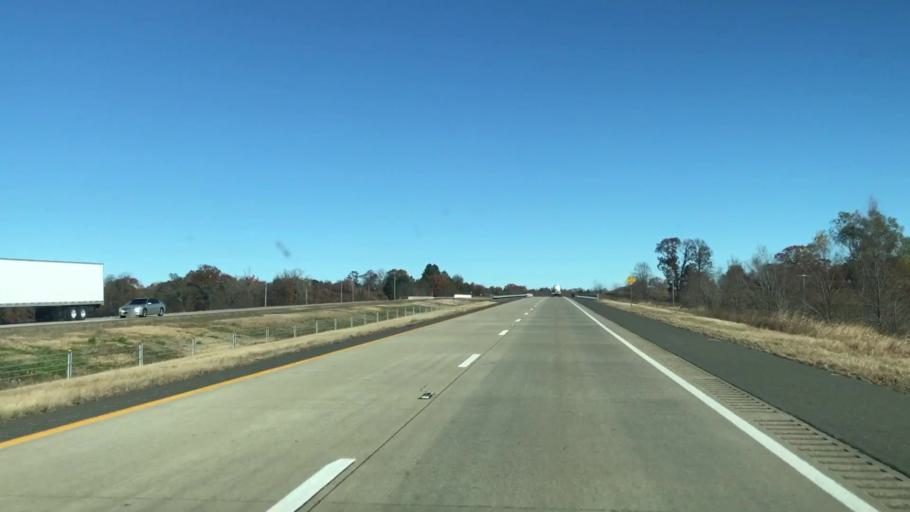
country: US
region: Texas
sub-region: Cass County
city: Queen City
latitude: 33.1511
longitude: -93.8906
